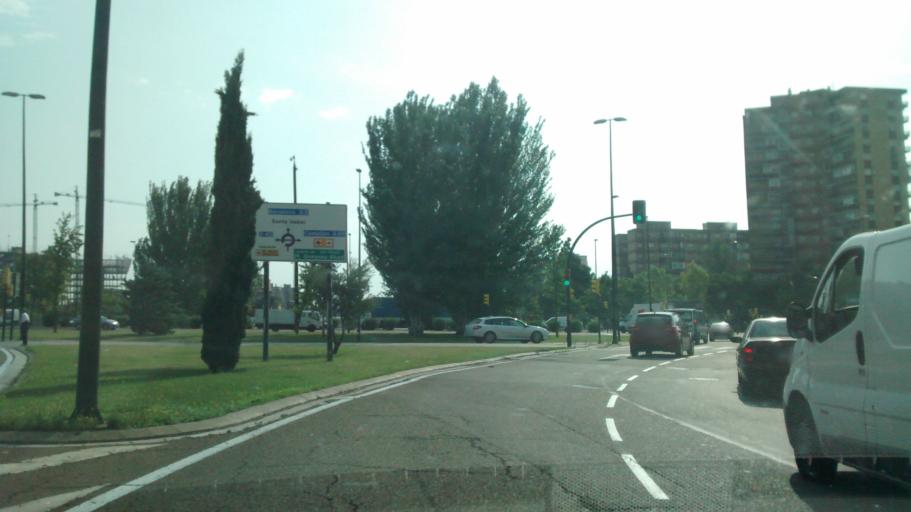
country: ES
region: Aragon
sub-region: Provincia de Zaragoza
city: Zaragoza
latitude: 41.6646
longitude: -0.8590
